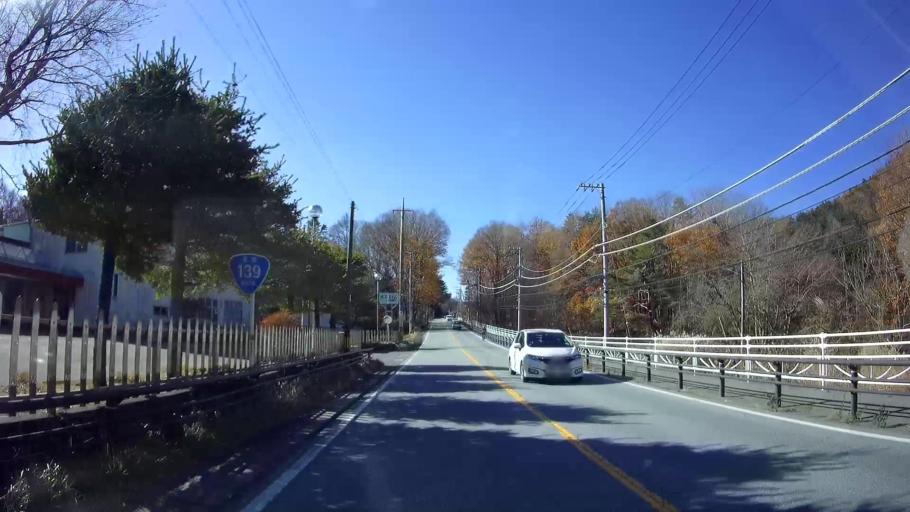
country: JP
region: Yamanashi
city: Fujikawaguchiko
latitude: 35.4835
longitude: 138.7159
